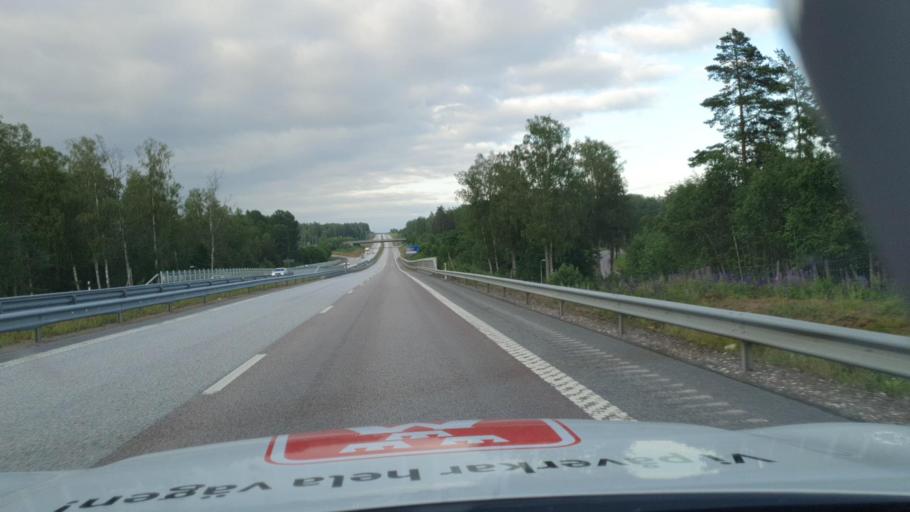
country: SE
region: Vaermland
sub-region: Karlstads Kommun
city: Skattkarr
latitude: 59.4006
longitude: 13.6027
